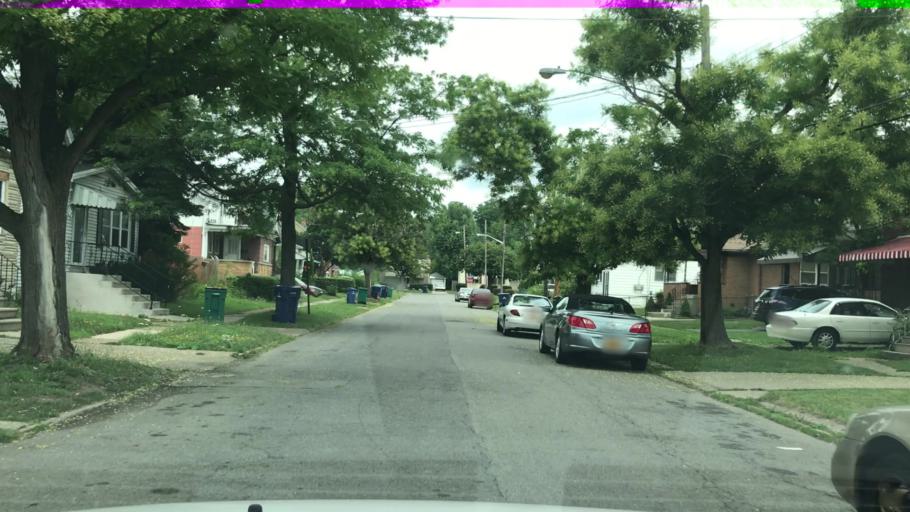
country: US
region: New York
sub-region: Erie County
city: Sloan
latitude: 42.9264
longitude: -78.8034
